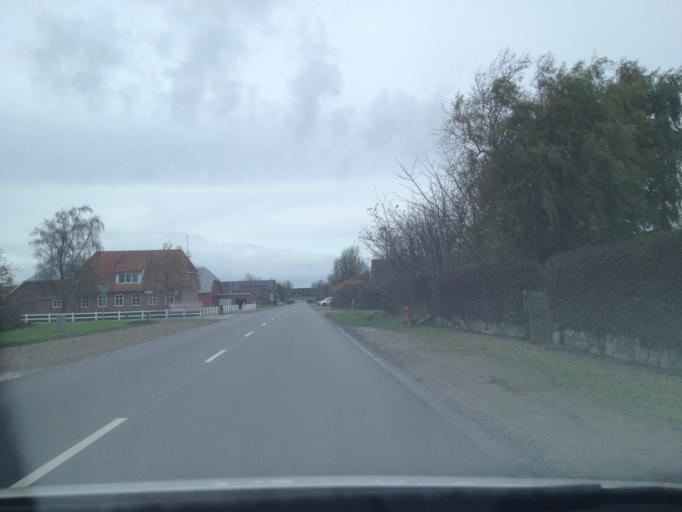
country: DK
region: South Denmark
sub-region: Esbjerg Kommune
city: Ribe
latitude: 55.2583
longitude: 8.8221
